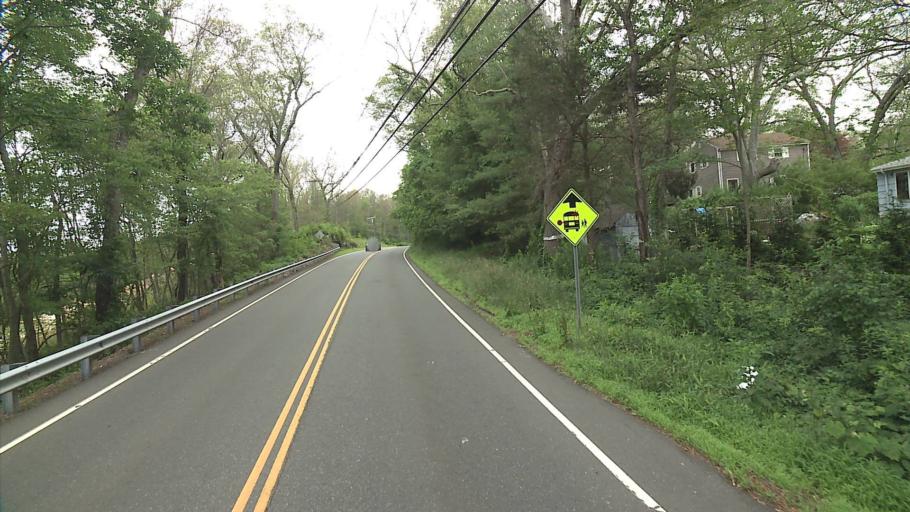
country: US
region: Connecticut
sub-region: New London County
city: Ledyard Center
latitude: 41.4515
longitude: -72.0174
